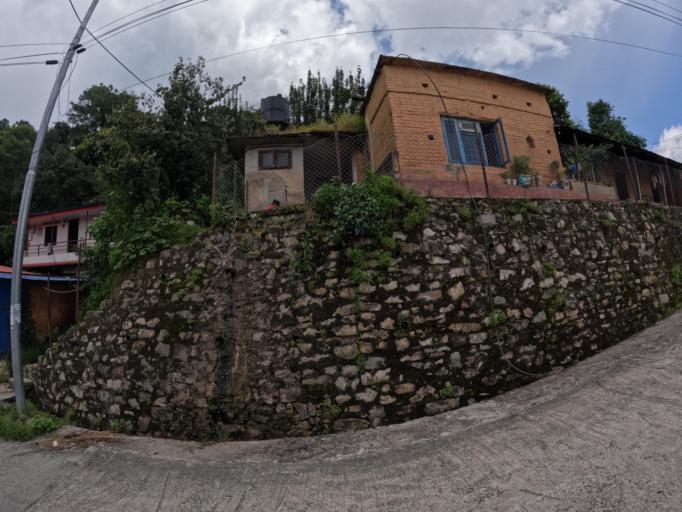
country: NP
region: Central Region
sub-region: Bagmati Zone
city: Kathmandu
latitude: 27.7768
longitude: 85.3403
